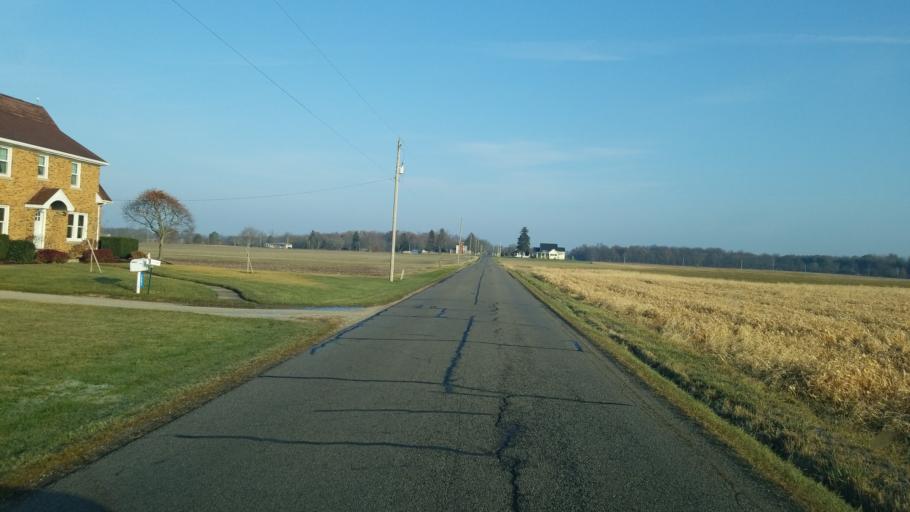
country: US
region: Ohio
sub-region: Crawford County
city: Bucyrus
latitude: 40.8081
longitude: -82.9020
